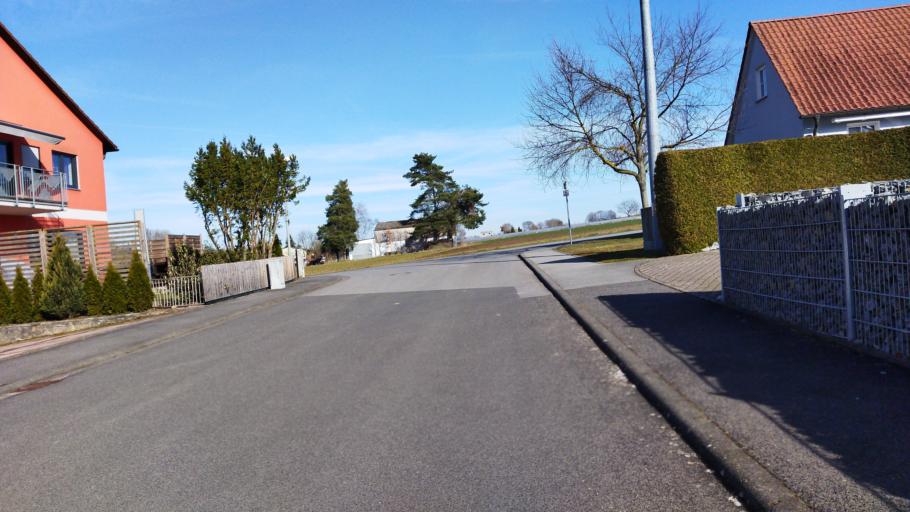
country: DE
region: Bavaria
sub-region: Regierungsbezirk Unterfranken
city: Wipfeld
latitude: 49.9430
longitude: 10.1857
